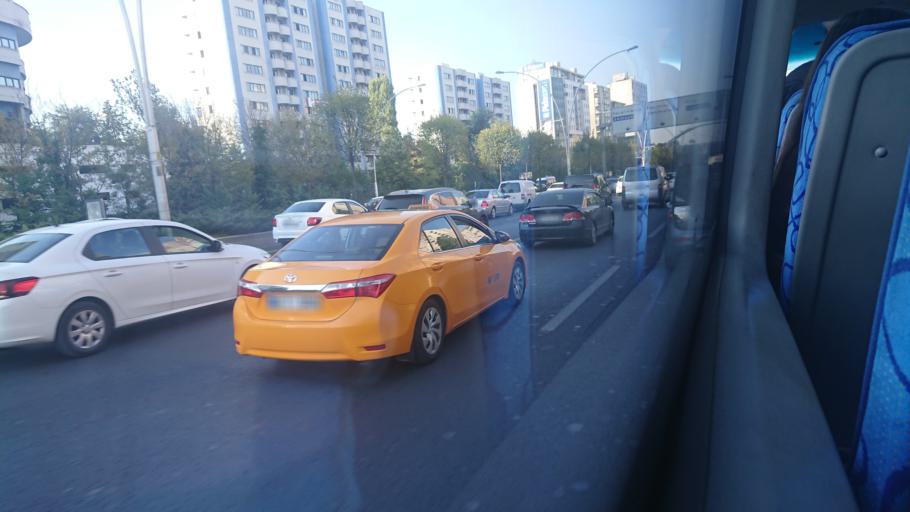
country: TR
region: Ankara
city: Ankara
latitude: 39.9266
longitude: 32.8164
